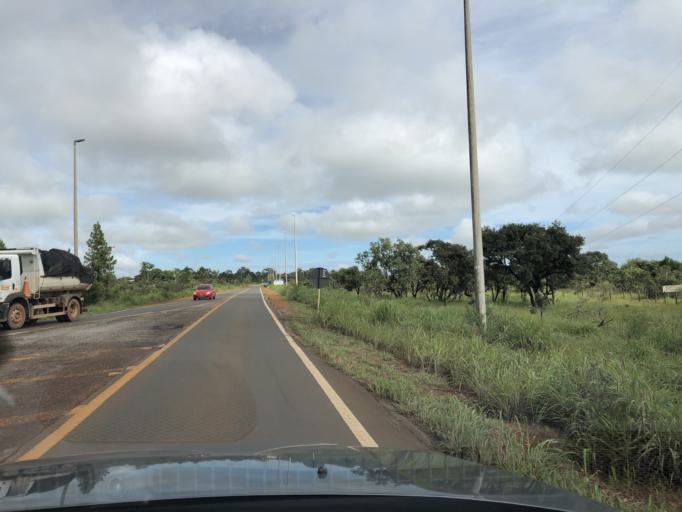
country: BR
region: Federal District
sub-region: Brasilia
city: Brasilia
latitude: -15.7344
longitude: -48.0776
